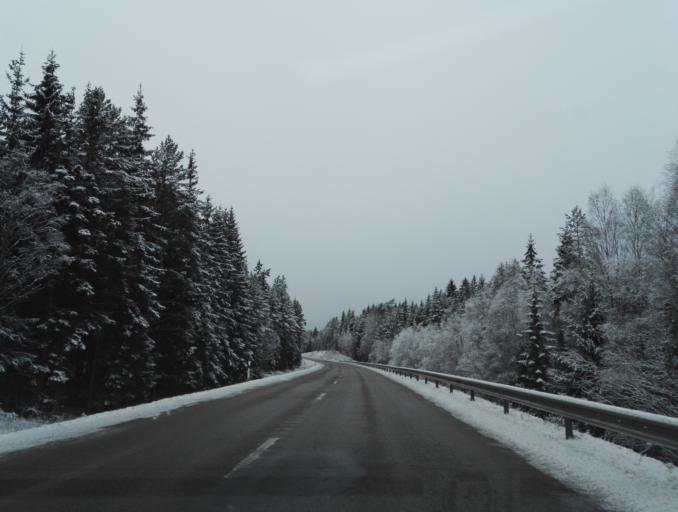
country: SE
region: Kronoberg
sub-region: Uppvidinge Kommun
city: Lenhovda
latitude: 57.1158
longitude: 15.2190
